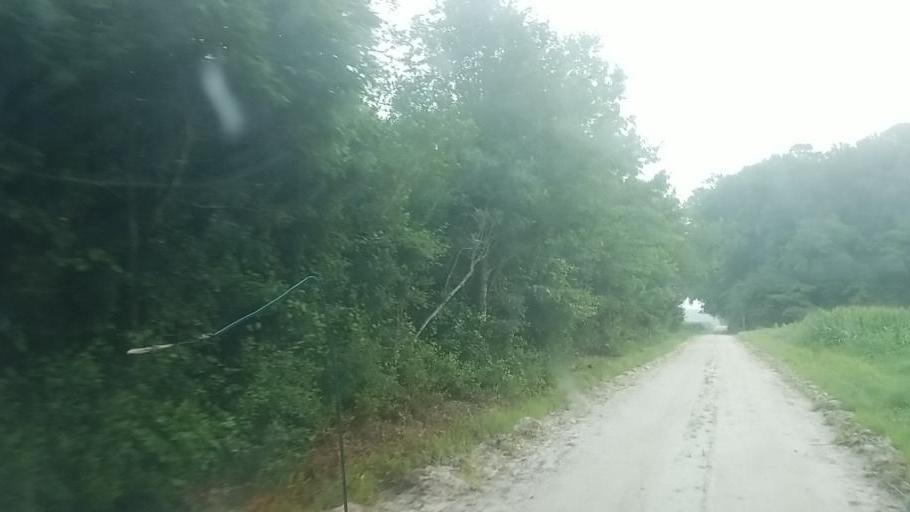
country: US
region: Maryland
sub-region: Wicomico County
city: Pittsville
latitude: 38.4444
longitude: -75.4377
